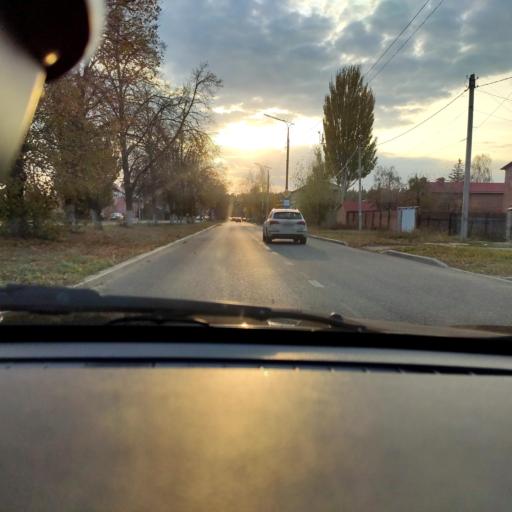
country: RU
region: Samara
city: Tol'yatti
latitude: 53.5170
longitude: 49.4015
